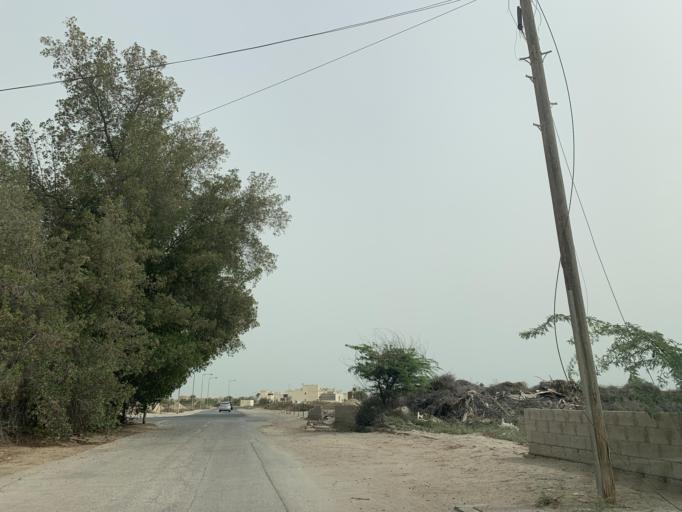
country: BH
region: Manama
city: Jidd Hafs
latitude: 26.2263
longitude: 50.5222
